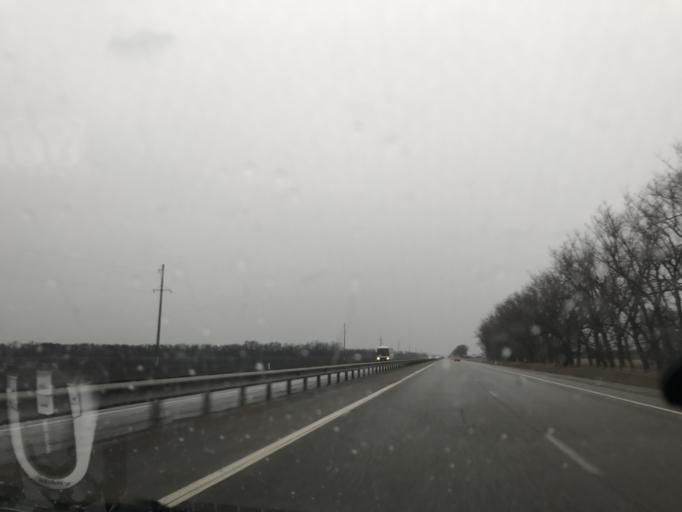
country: RU
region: Krasnodarskiy
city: Kislyakovskaya
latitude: 46.3663
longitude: 39.7583
